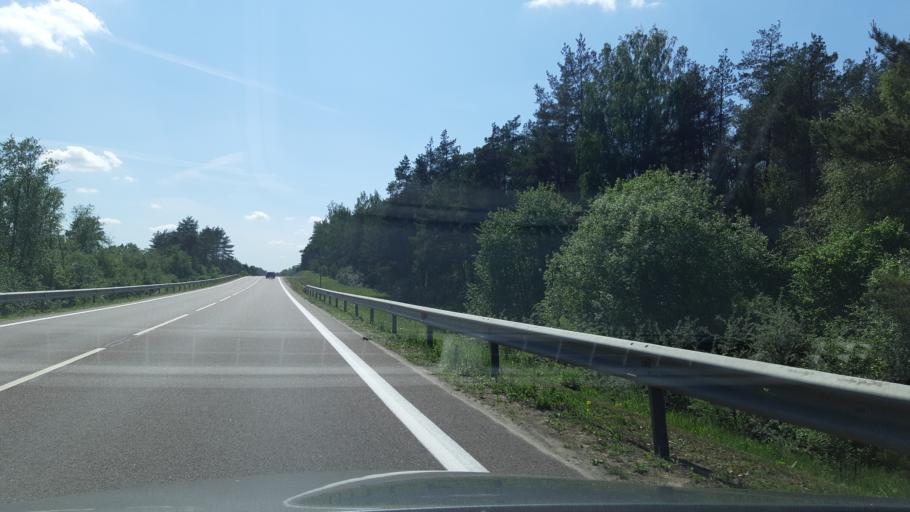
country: LT
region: Vilnius County
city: Ukmerge
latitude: 55.2951
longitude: 24.8490
